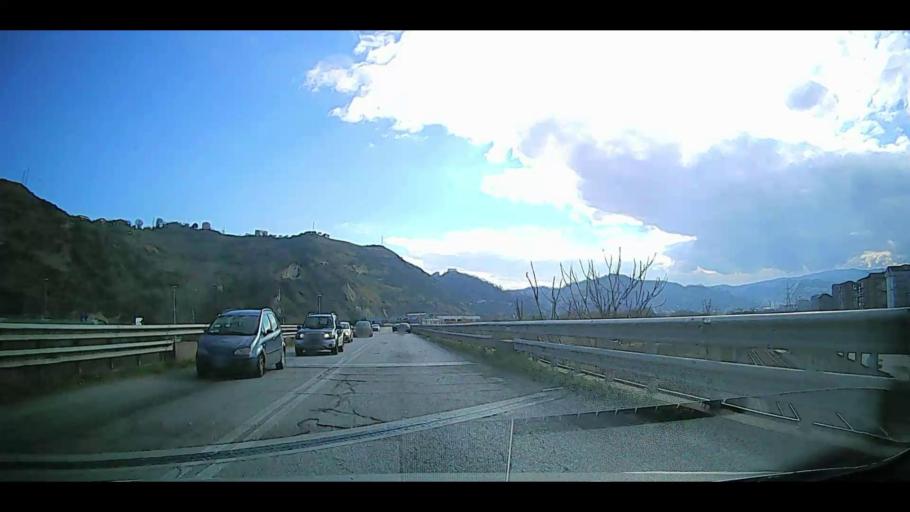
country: IT
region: Calabria
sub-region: Provincia di Cosenza
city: Cosenza
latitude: 39.3125
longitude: 16.2605
